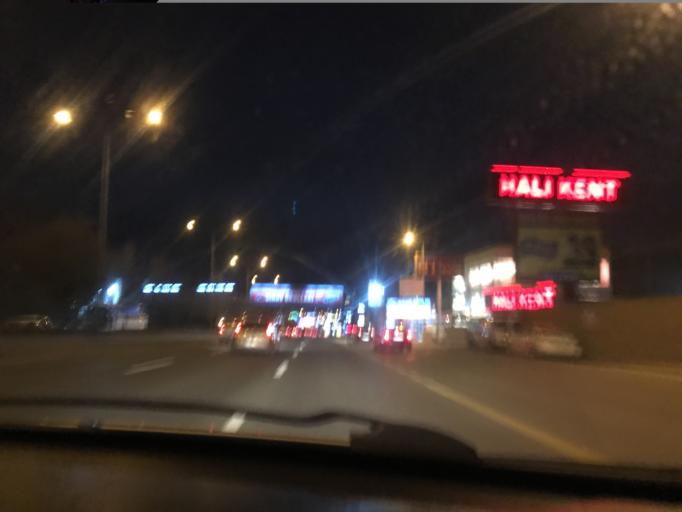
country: TR
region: Ankara
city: Batikent
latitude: 39.9455
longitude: 32.7270
